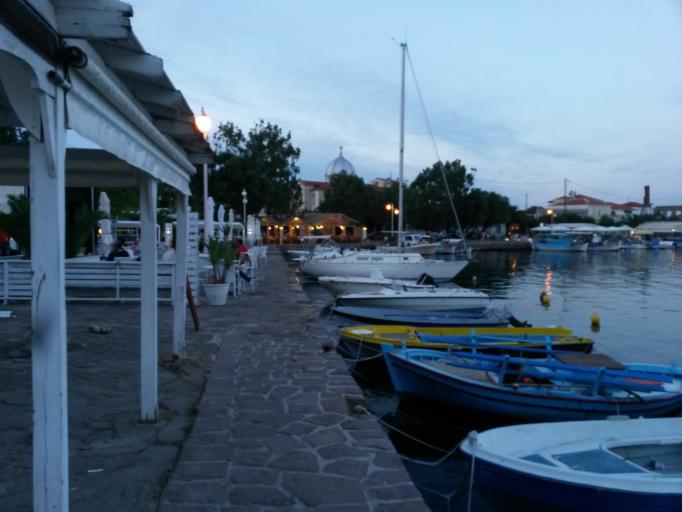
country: GR
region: North Aegean
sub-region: Nomos Lesvou
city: Pamfylla
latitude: 39.1441
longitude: 26.5293
